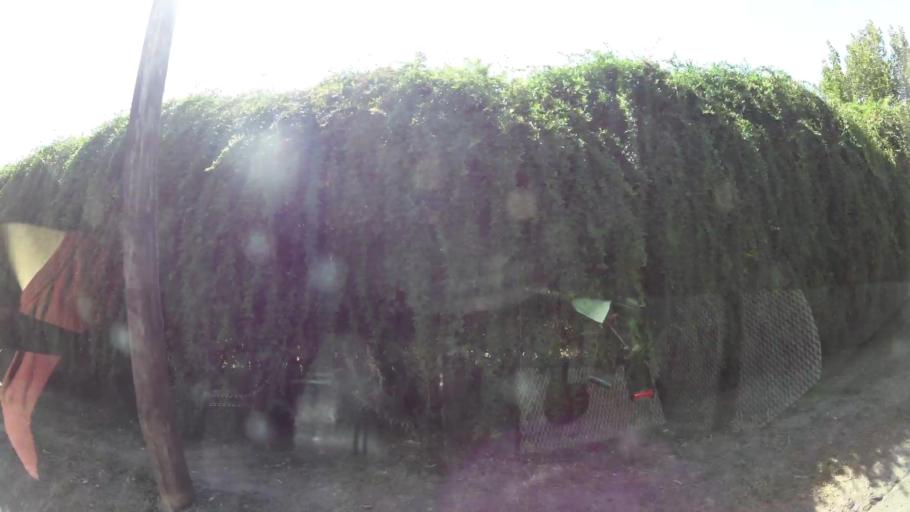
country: AR
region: Cordoba
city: Villa Allende
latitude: -31.2937
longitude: -64.2815
